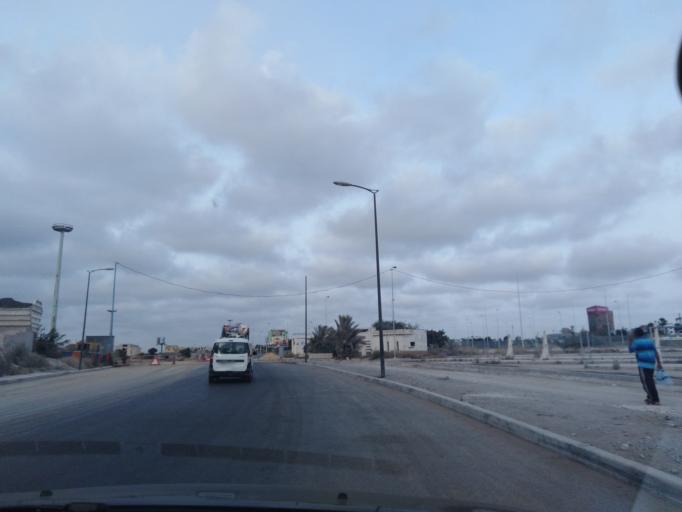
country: MA
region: Grand Casablanca
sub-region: Casablanca
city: Casablanca
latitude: 33.5458
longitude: -7.6476
